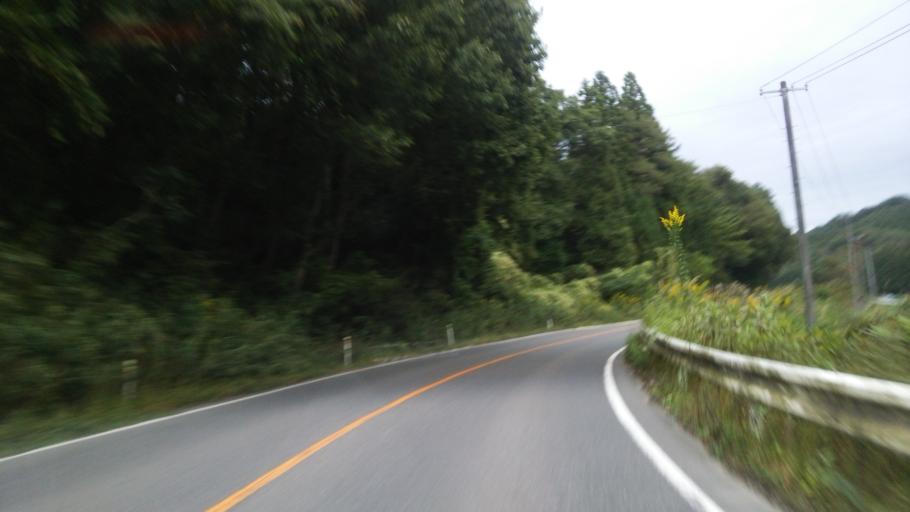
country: JP
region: Fukushima
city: Sukagawa
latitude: 37.2240
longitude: 140.2483
